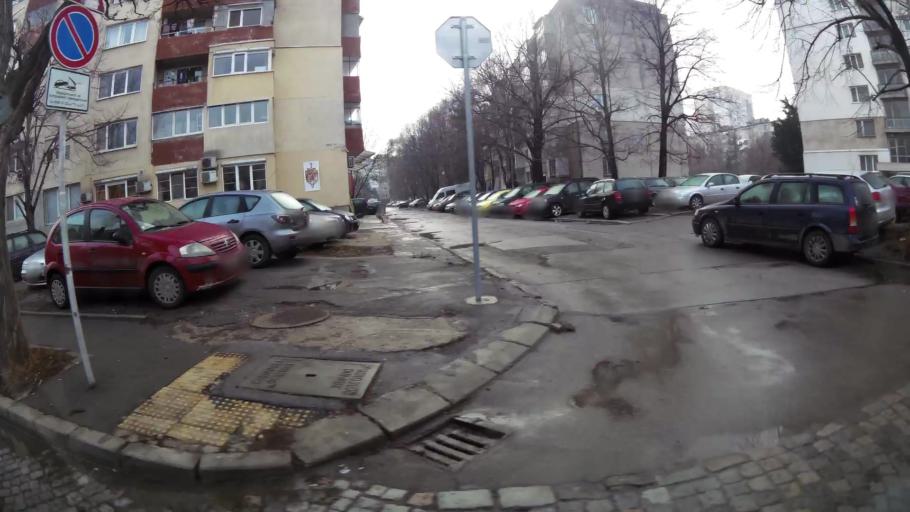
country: BG
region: Sofia-Capital
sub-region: Stolichna Obshtina
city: Sofia
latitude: 42.7288
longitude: 23.3088
